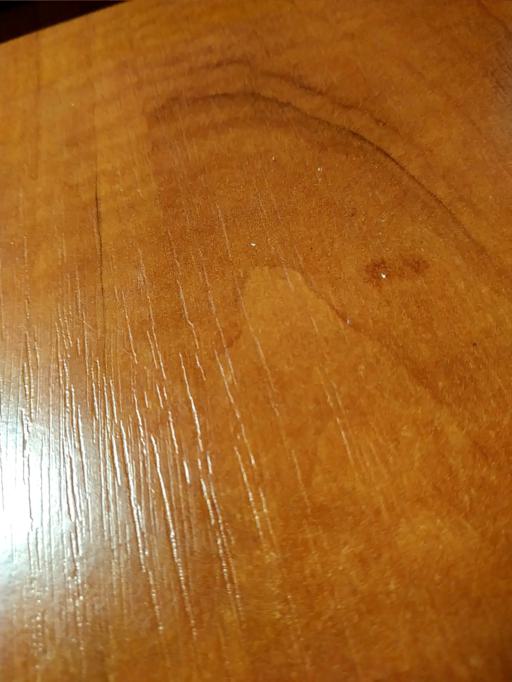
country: RU
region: Tverskaya
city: Zubtsov
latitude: 56.1573
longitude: 34.6484
